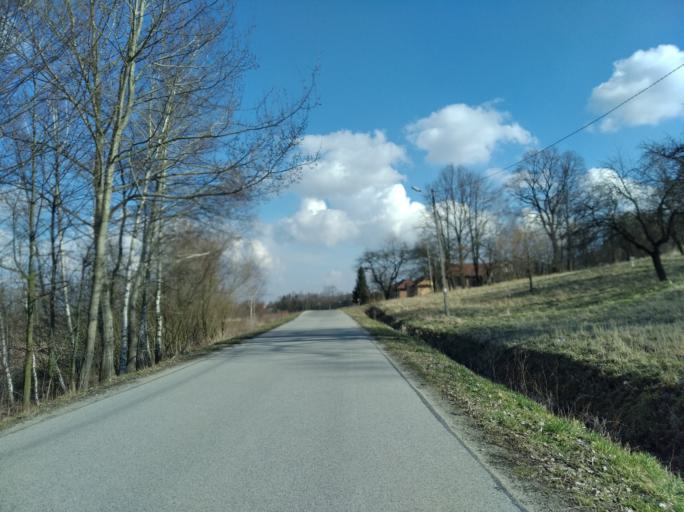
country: PL
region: Subcarpathian Voivodeship
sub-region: Powiat strzyzowski
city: Wisniowa
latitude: 49.8587
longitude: 21.6472
